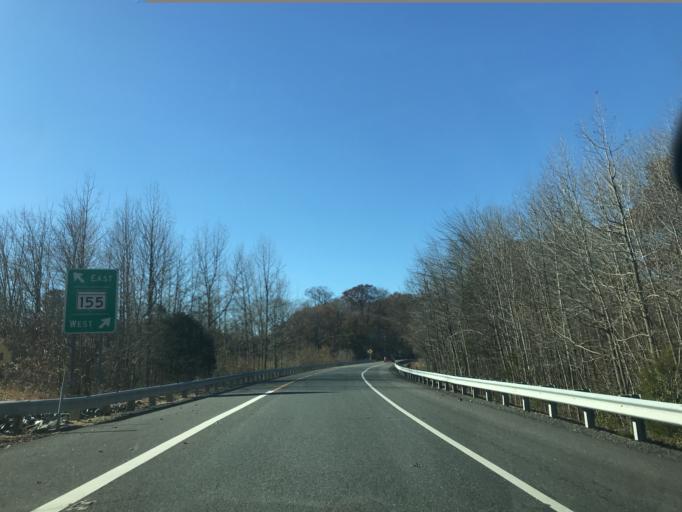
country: US
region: Maryland
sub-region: Harford County
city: Havre de Grace
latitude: 39.5735
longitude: -76.1398
